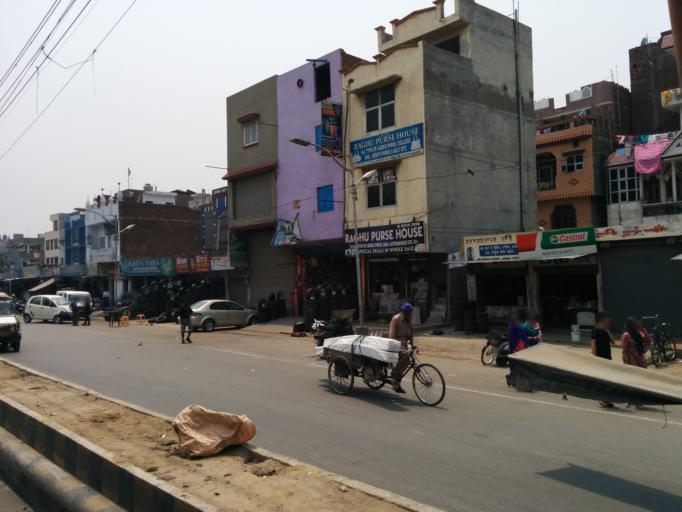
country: IN
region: Punjab
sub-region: Amritsar
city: Amritsar
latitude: 31.6289
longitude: 74.8818
